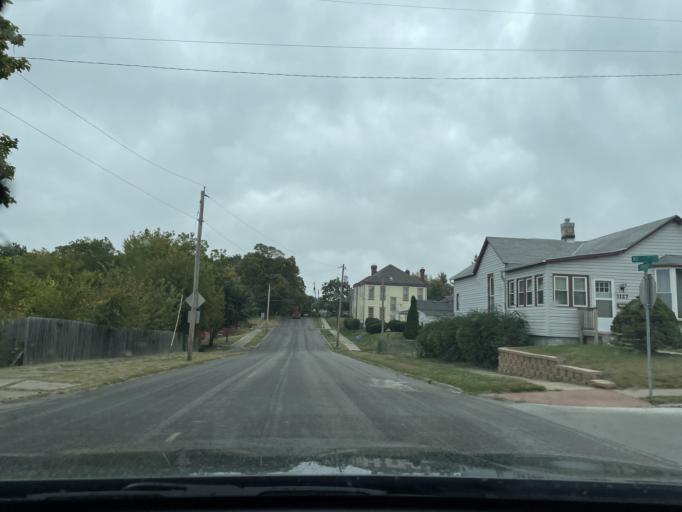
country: US
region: Missouri
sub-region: Buchanan County
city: Saint Joseph
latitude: 39.7769
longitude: -94.8374
